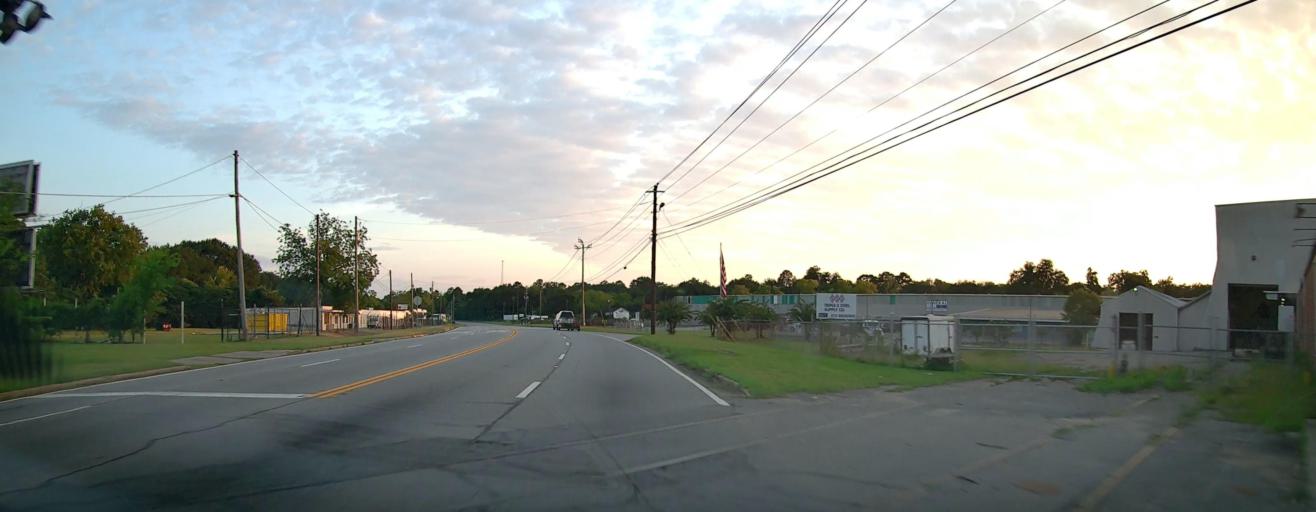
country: US
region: Georgia
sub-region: Bibb County
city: Macon
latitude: 32.7923
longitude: -83.6499
